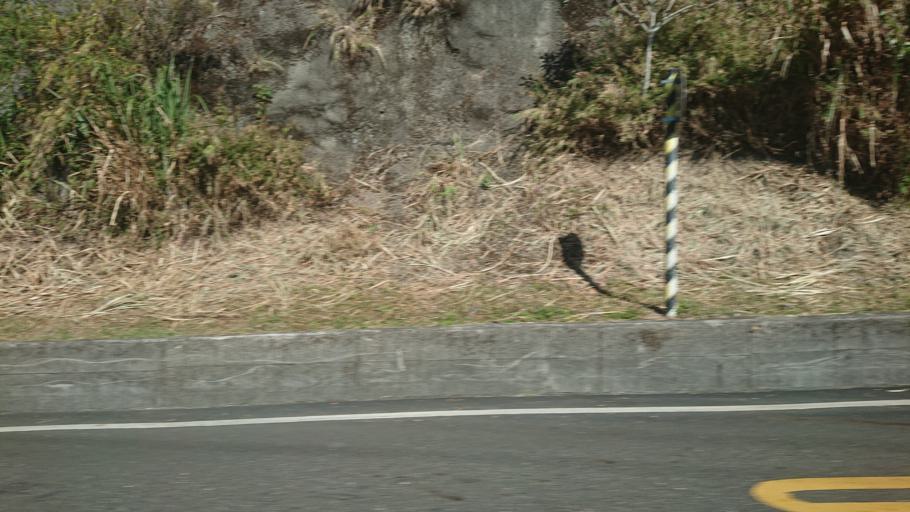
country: TW
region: Taiwan
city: Lugu
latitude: 23.4723
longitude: 120.7339
